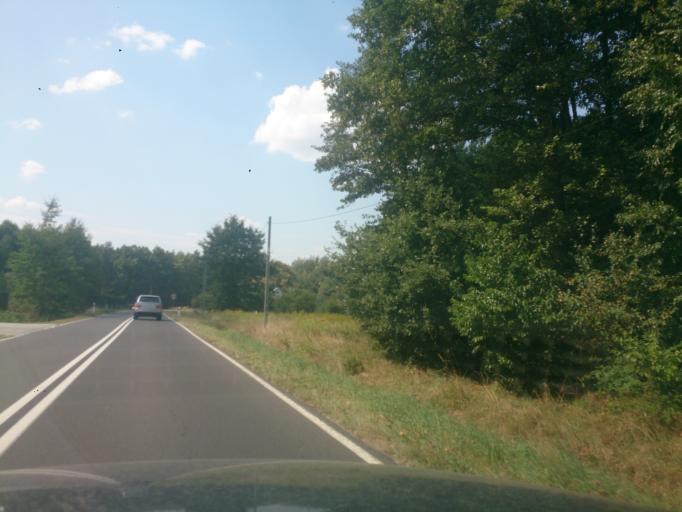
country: PL
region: Subcarpathian Voivodeship
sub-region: Powiat kolbuszowski
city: Majdan Krolewski
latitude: 50.3910
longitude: 21.6970
